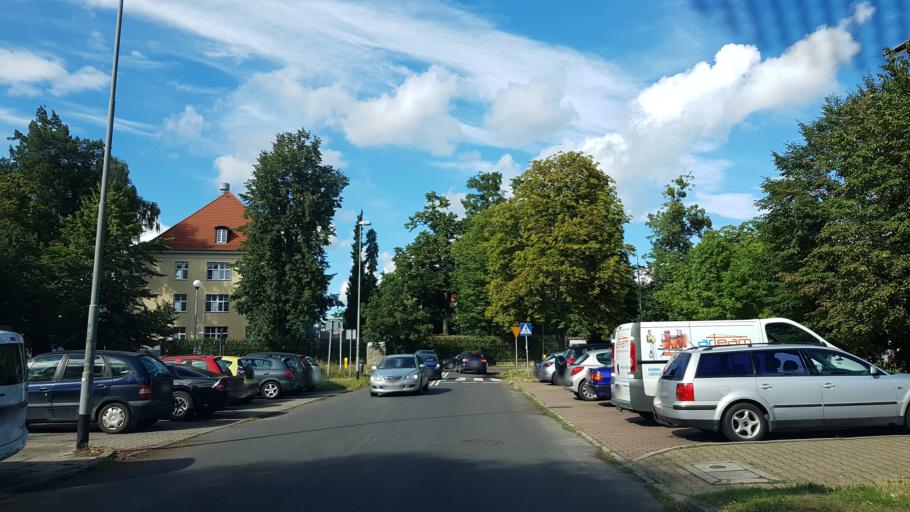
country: PL
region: West Pomeranian Voivodeship
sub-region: Szczecin
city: Szczecin
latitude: 53.4416
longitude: 14.4922
